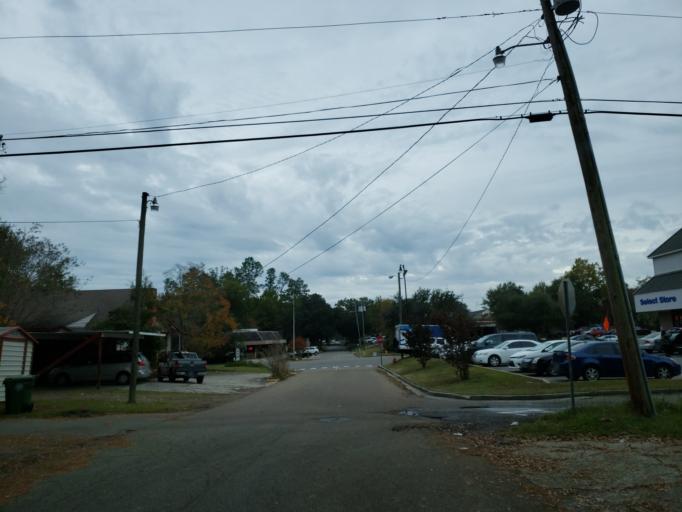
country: US
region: Mississippi
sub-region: Forrest County
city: Hattiesburg
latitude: 31.3254
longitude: -89.3252
